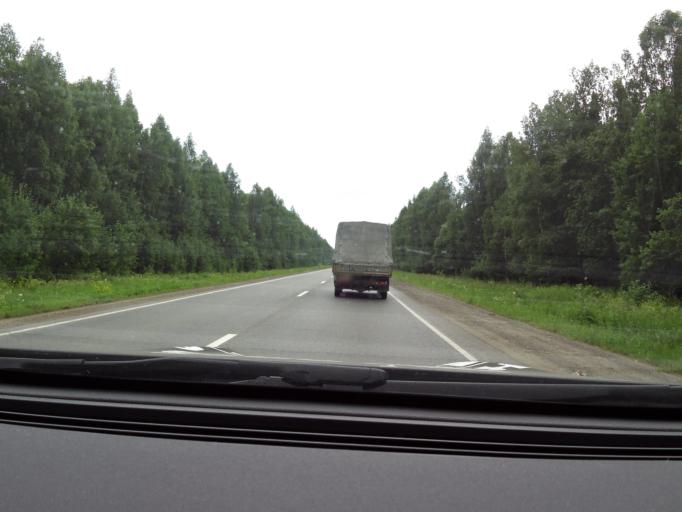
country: RU
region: Perm
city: Kukushtan
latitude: 57.5757
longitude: 56.5592
